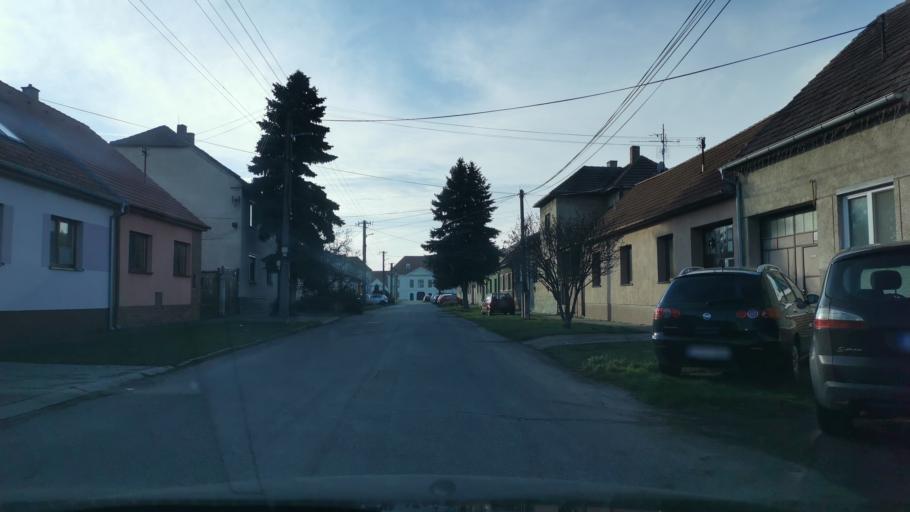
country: SK
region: Trnavsky
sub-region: Okres Skalica
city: Holic
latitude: 48.7838
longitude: 17.1070
